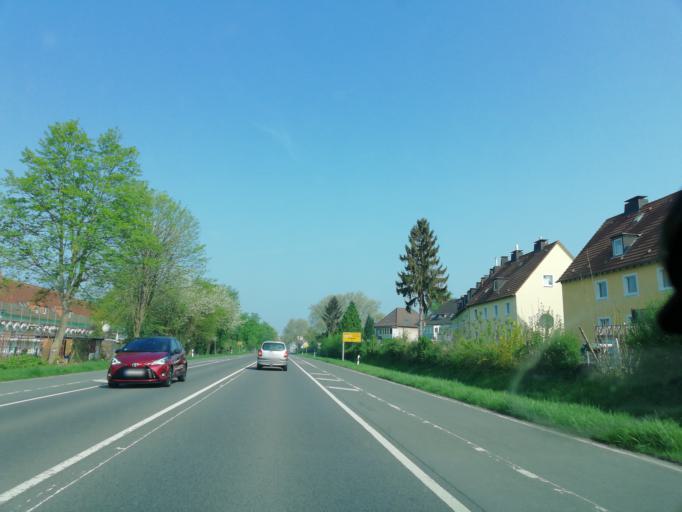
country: DE
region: North Rhine-Westphalia
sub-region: Regierungsbezirk Arnsberg
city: Dortmund
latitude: 51.4787
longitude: 7.4444
